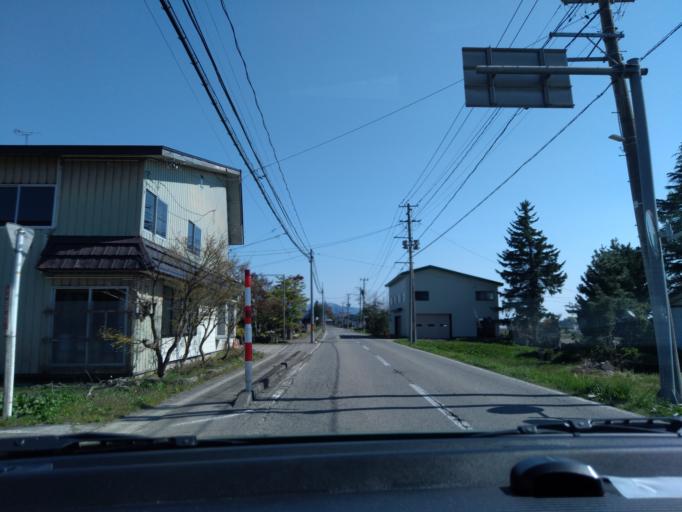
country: JP
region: Akita
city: Kakunodatemachi
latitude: 39.5211
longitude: 140.5884
